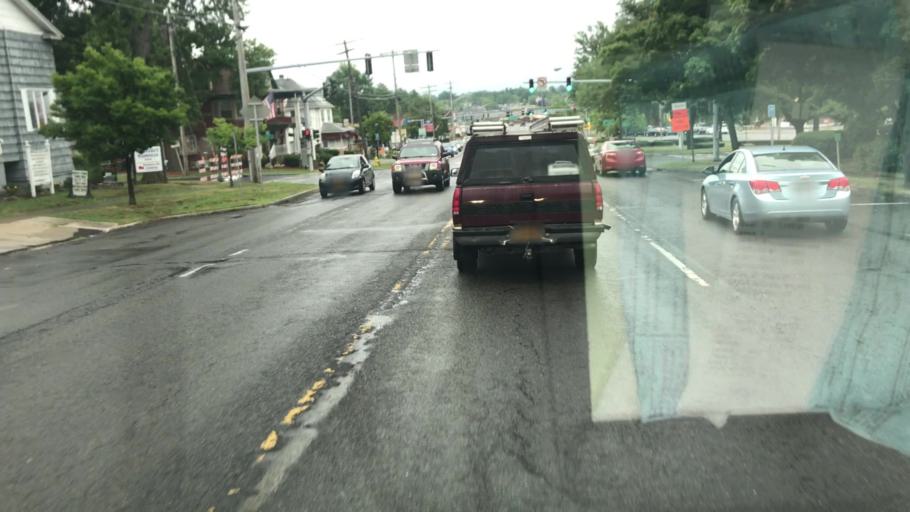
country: US
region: New York
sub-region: Onondaga County
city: Liverpool
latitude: 43.1037
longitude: -76.2067
